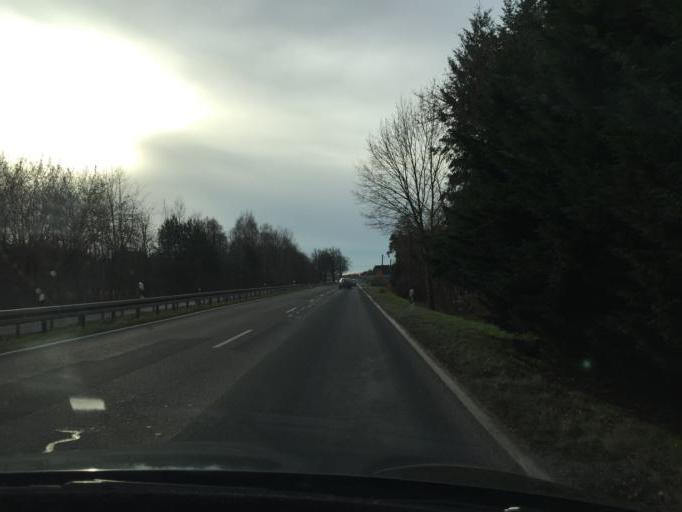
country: DE
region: Brandenburg
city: Cottbus
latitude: 51.7932
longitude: 14.3782
